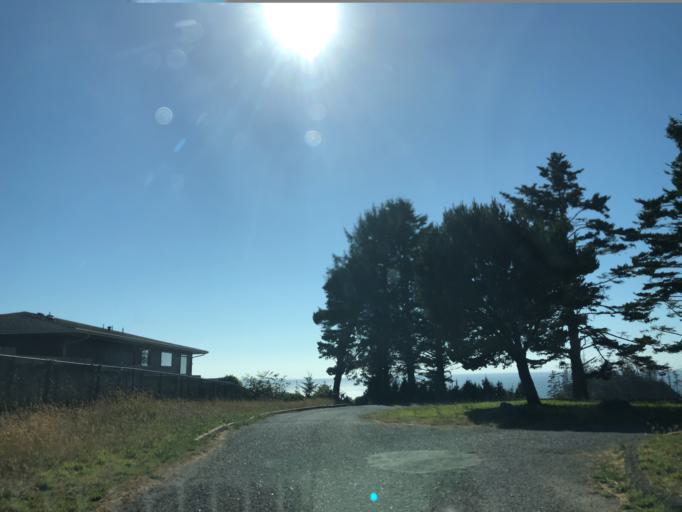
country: US
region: California
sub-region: Humboldt County
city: Westhaven-Moonstone
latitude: 41.0611
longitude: -124.1460
